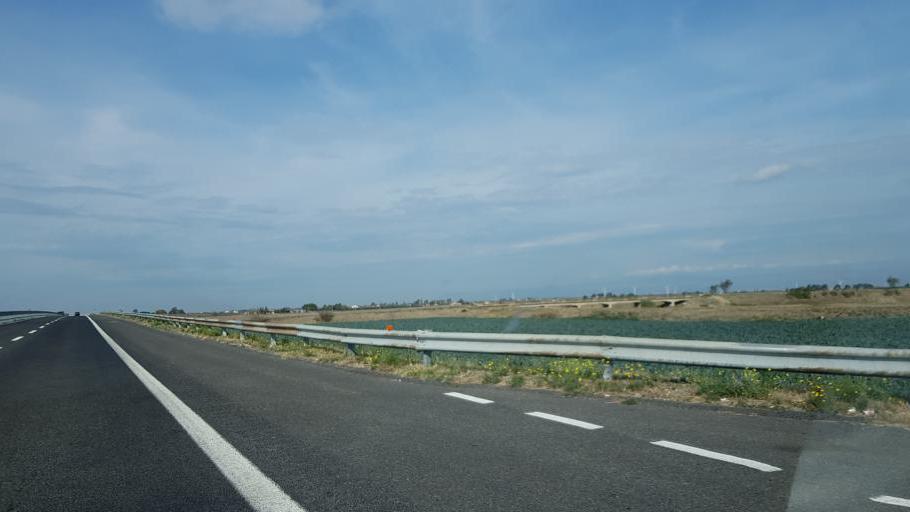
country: IT
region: Apulia
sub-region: Provincia di Foggia
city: Carapelle
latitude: 41.3775
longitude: 15.7589
